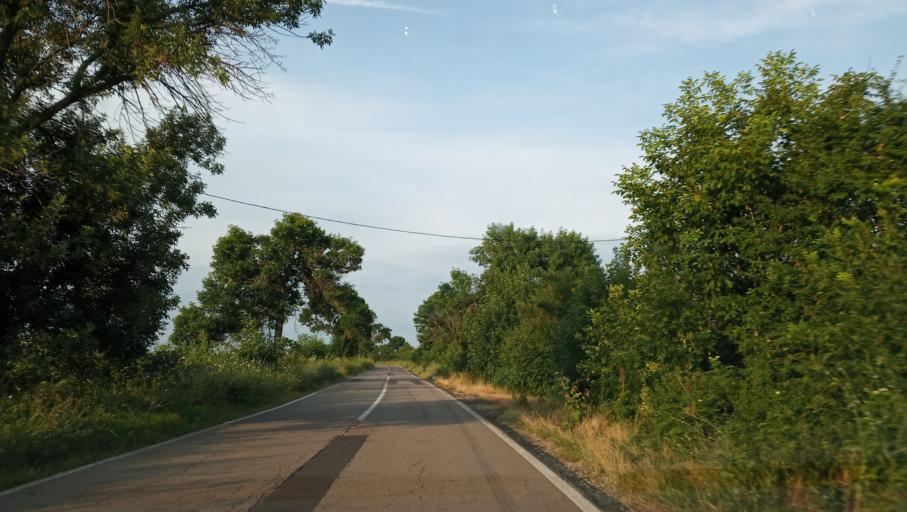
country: RO
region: Giurgiu
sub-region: Comuna Greaca
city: Greaca
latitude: 44.1166
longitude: 26.3637
